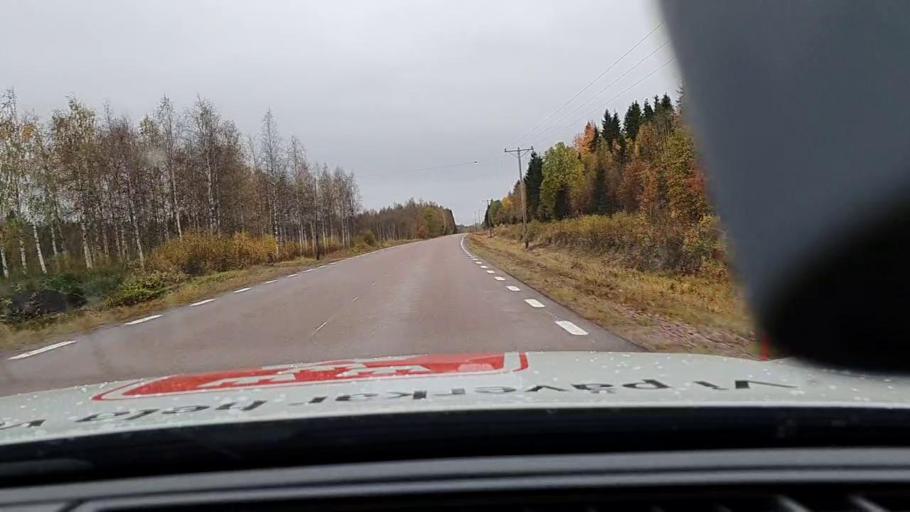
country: FI
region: Lapland
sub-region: Torniolaakso
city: Ylitornio
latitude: 66.1276
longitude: 23.9107
